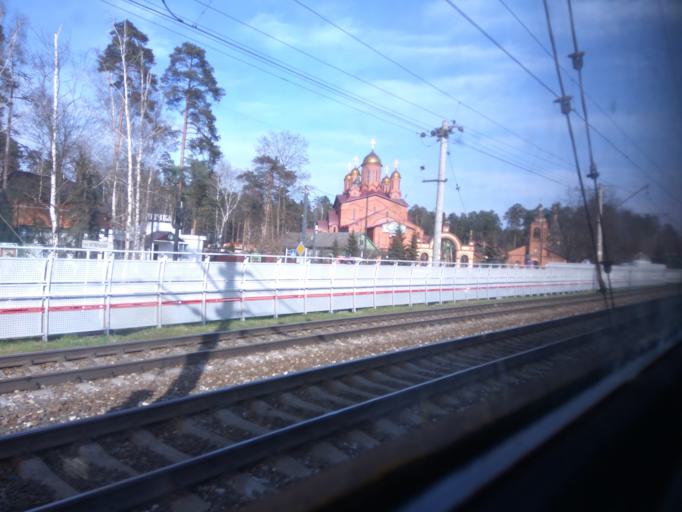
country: RU
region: Moskovskaya
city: Il'inskiy
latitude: 55.6165
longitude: 38.1004
